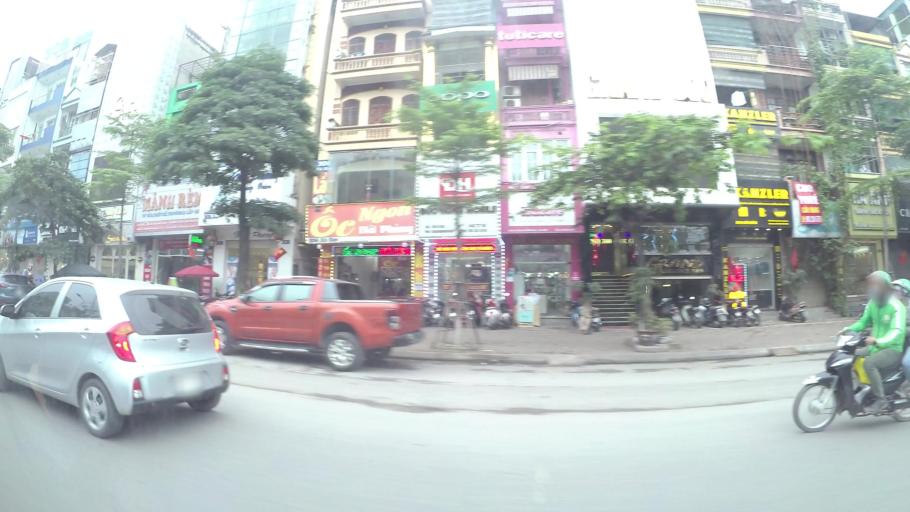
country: VN
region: Ha Noi
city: Dong Da
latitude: 21.0133
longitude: 105.8355
